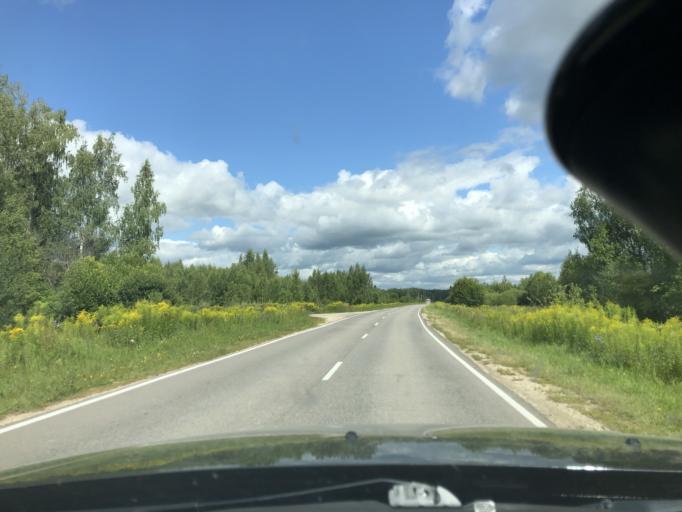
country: RU
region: Tula
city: Revyakino
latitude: 54.4141
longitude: 37.6931
